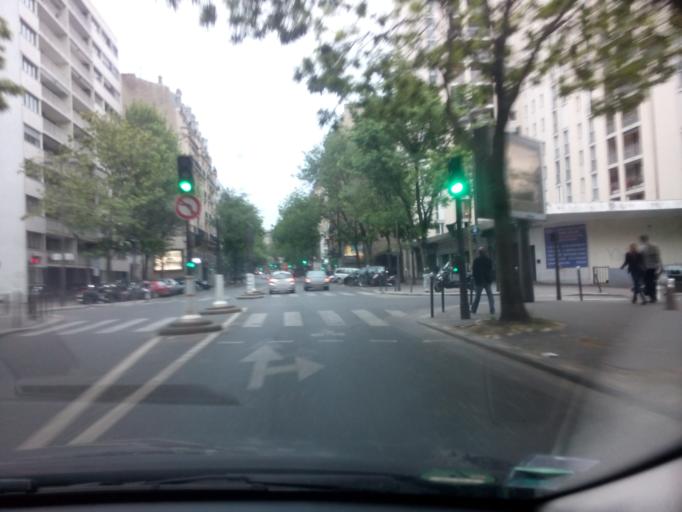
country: FR
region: Ile-de-France
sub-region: Departement du Val-de-Marne
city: Gentilly
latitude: 48.8262
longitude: 2.3437
